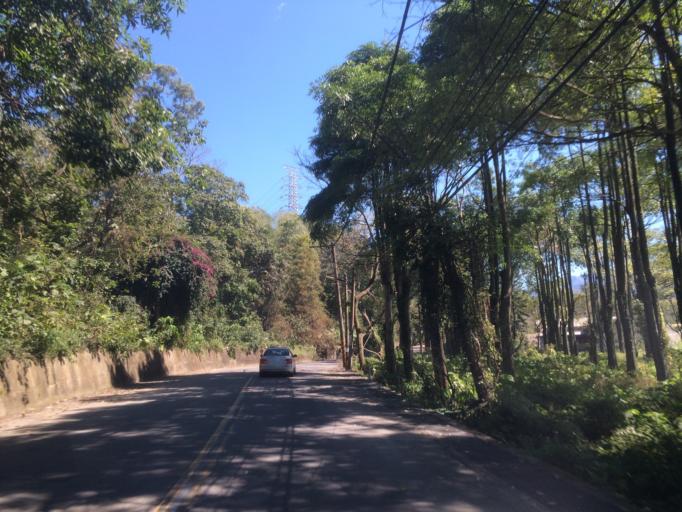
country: TW
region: Taiwan
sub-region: Yunlin
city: Douliu
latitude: 23.7002
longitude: 120.6145
